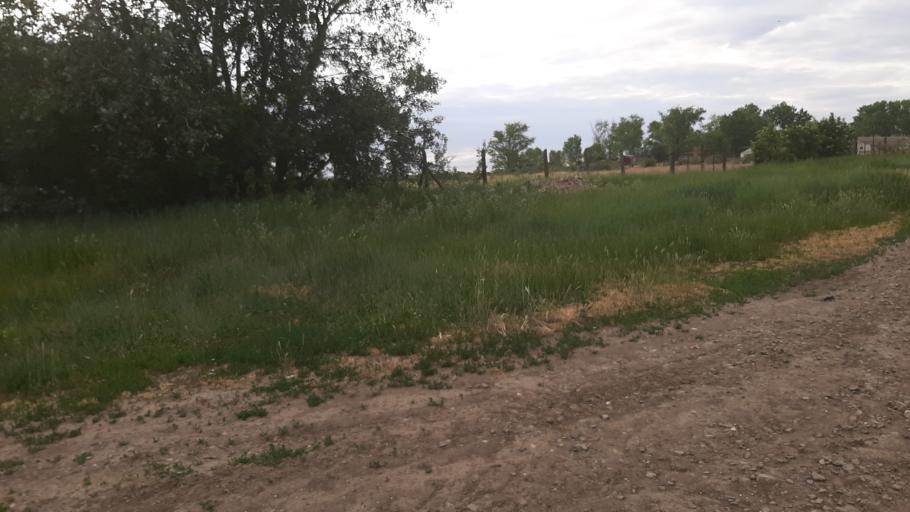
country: HU
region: Csongrad
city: Deszk
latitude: 46.1686
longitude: 20.1783
